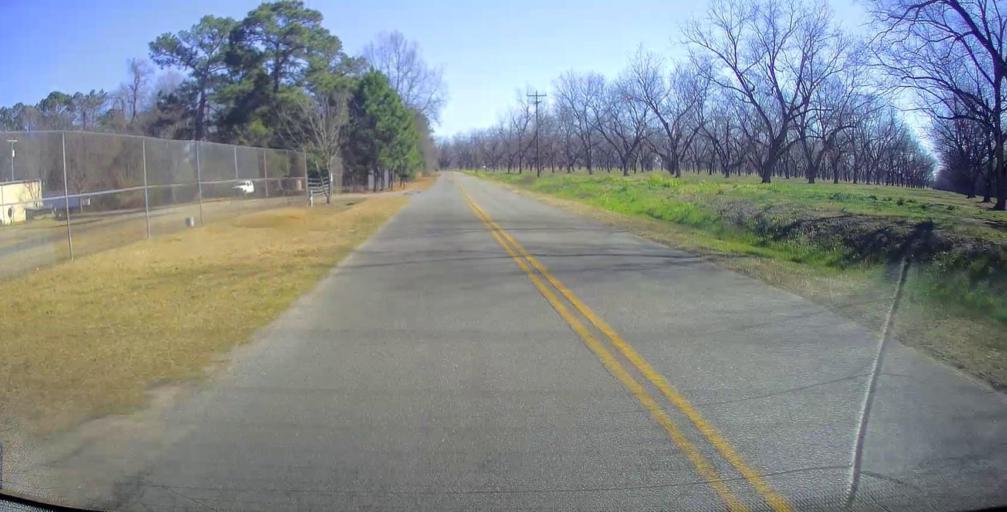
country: US
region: Georgia
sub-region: Peach County
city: Fort Valley
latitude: 32.6316
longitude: -83.8508
